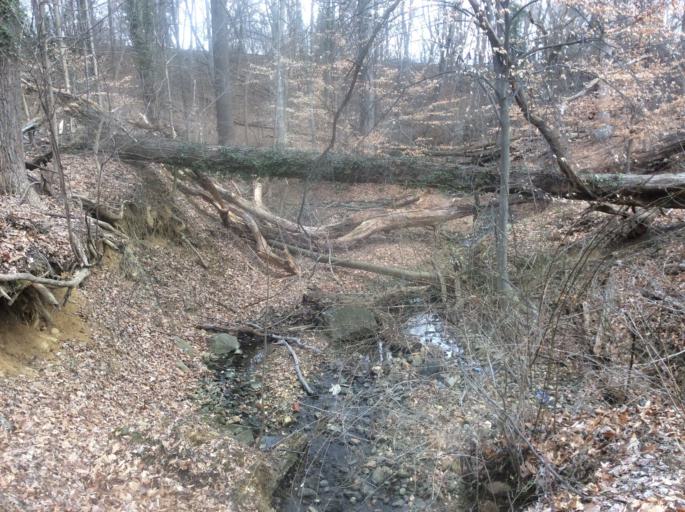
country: US
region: Maryland
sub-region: Baltimore County
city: Catonsville
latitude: 39.2689
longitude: -76.7219
